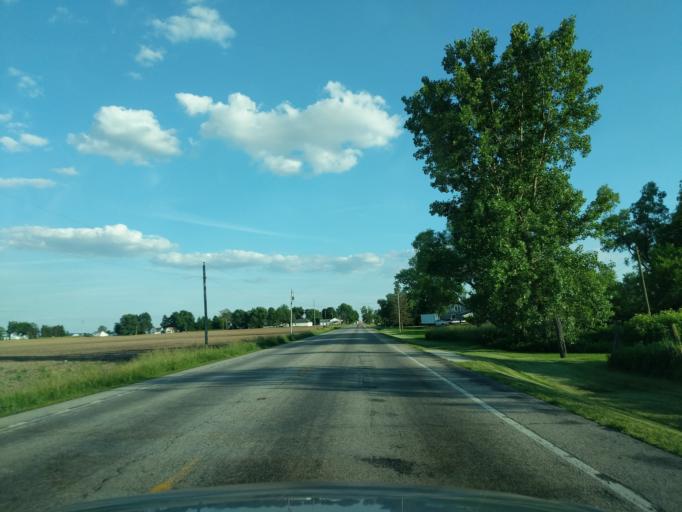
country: US
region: Indiana
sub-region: Huntington County
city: Warren
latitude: 40.7752
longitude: -85.4548
